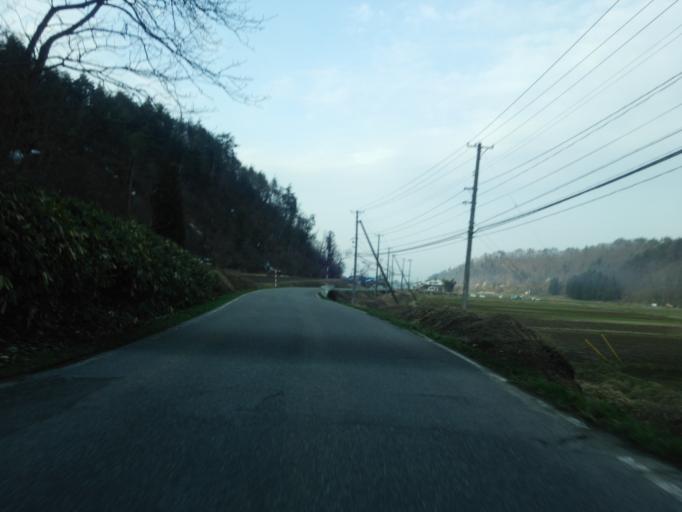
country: JP
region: Fukushima
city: Kitakata
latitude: 37.6916
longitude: 139.9082
